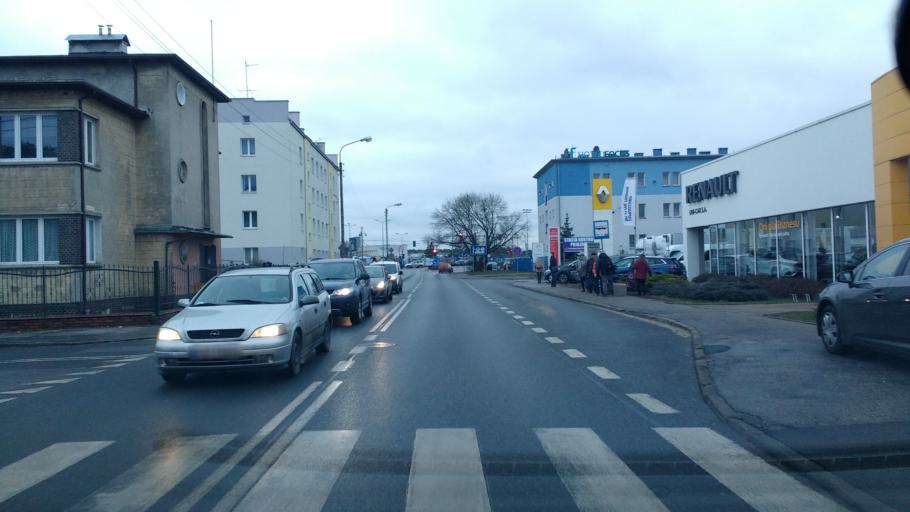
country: PL
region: Kujawsko-Pomorskie
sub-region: Bydgoszcz
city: Bydgoszcz
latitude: 53.1453
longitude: 18.0260
